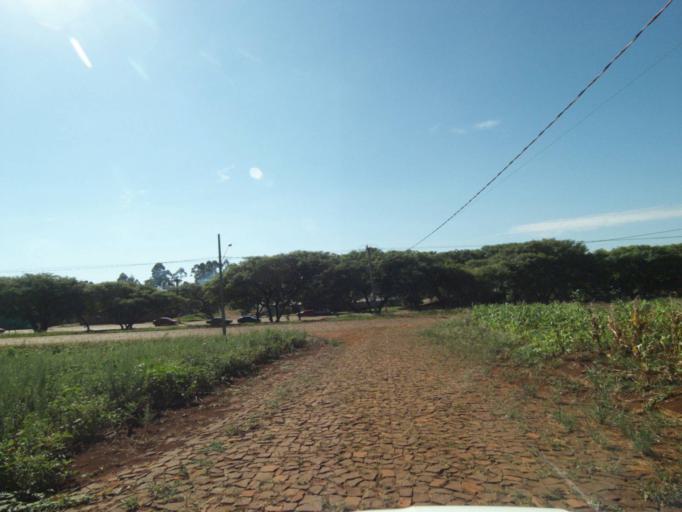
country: BR
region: Parana
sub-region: Laranjeiras Do Sul
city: Laranjeiras do Sul
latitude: -25.4857
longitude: -52.5235
